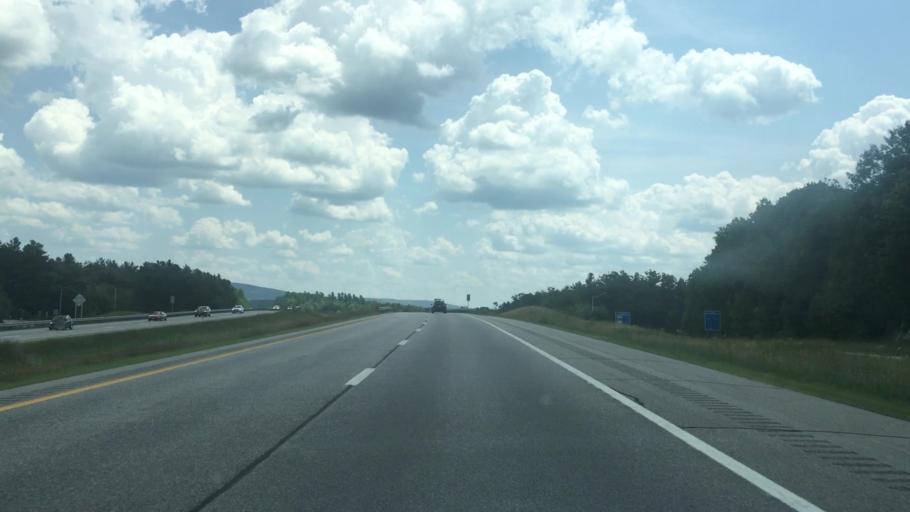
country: US
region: New Hampshire
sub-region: Merrimack County
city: New London
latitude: 43.4247
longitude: -72.0388
